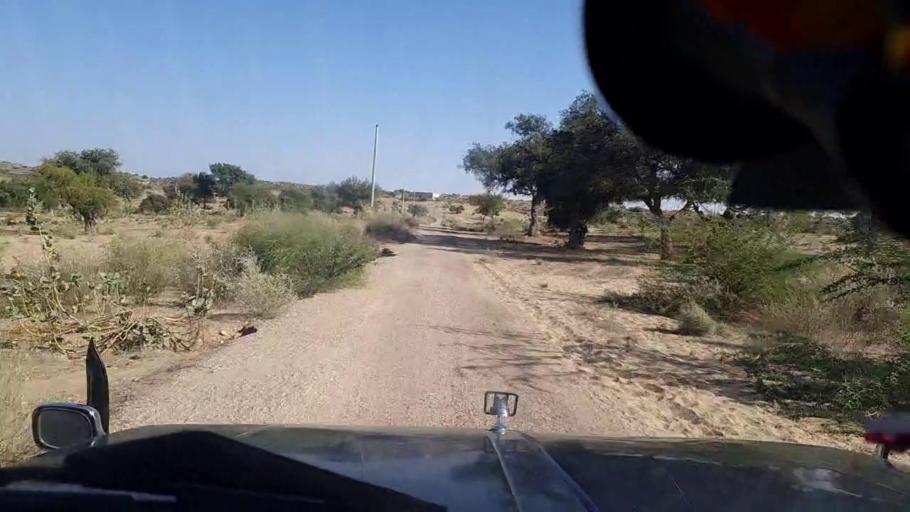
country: PK
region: Sindh
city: Diplo
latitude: 24.4696
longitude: 69.8062
